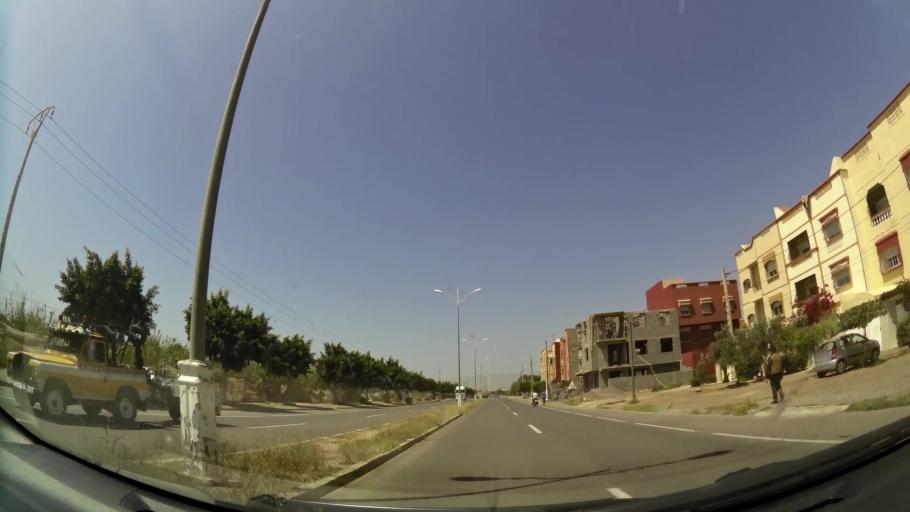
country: MA
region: Souss-Massa-Draa
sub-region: Inezgane-Ait Mellou
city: Inezgane
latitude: 30.3501
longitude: -9.4863
